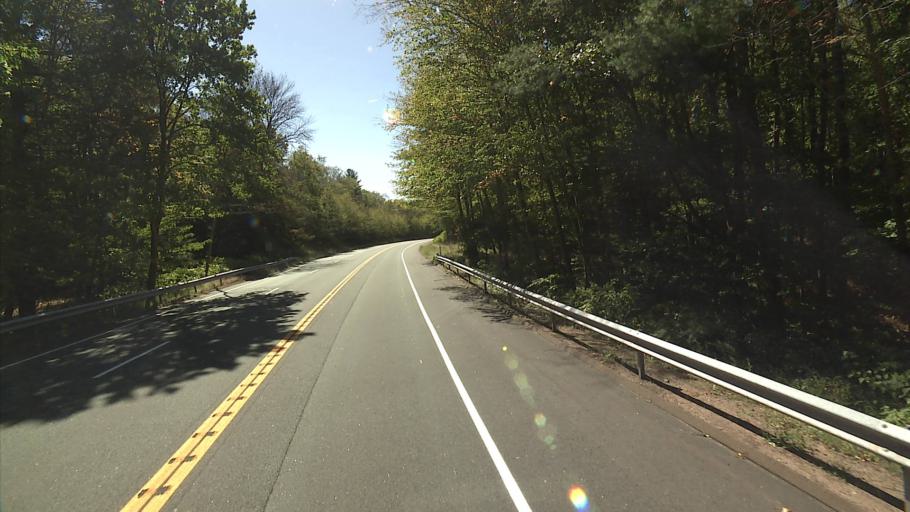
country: US
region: Connecticut
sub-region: New Haven County
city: Woodbridge
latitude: 41.3914
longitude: -72.9719
